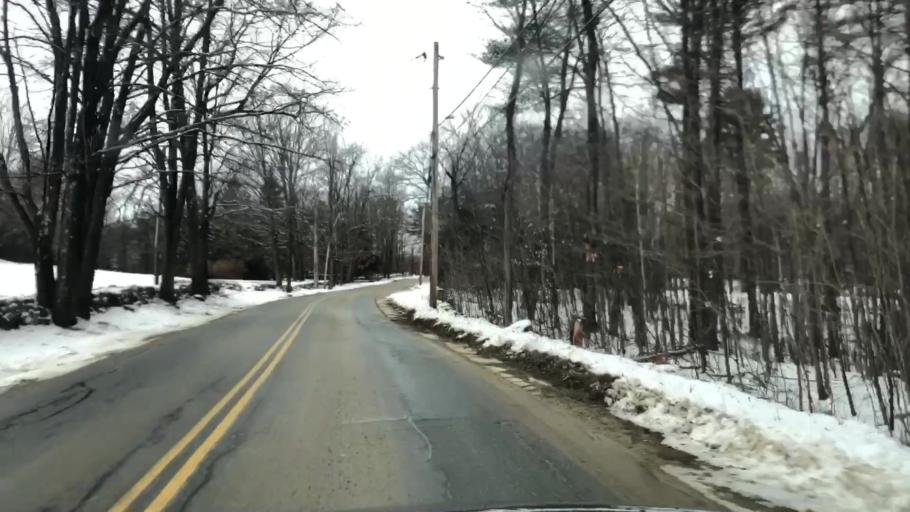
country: US
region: New Hampshire
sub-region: Hillsborough County
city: Mont Vernon
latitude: 42.9206
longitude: -71.5994
